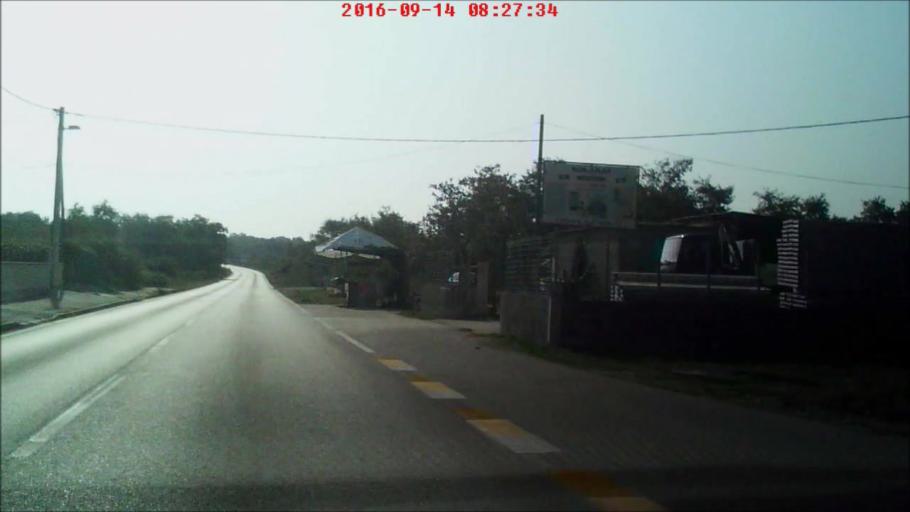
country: HR
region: Zadarska
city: Zadar
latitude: 44.1881
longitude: 15.2675
